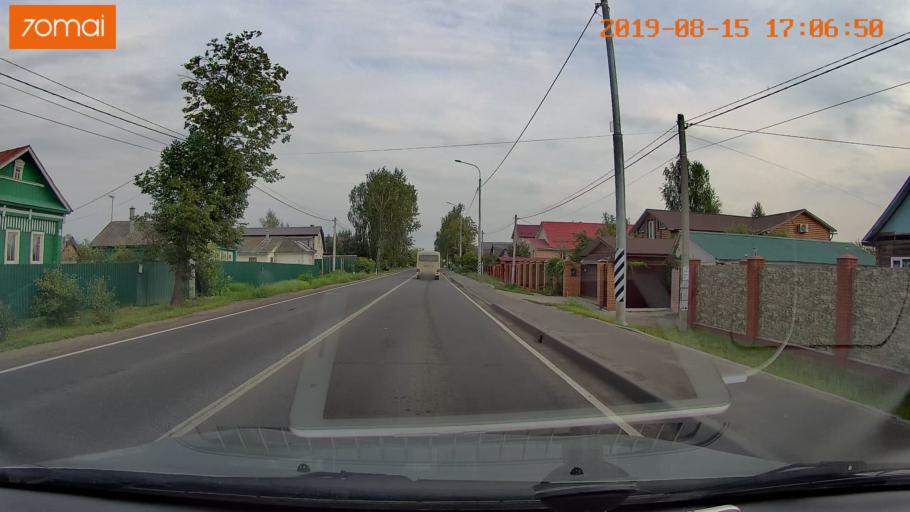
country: RU
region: Moskovskaya
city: Beloozerskiy
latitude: 55.4679
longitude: 38.4168
